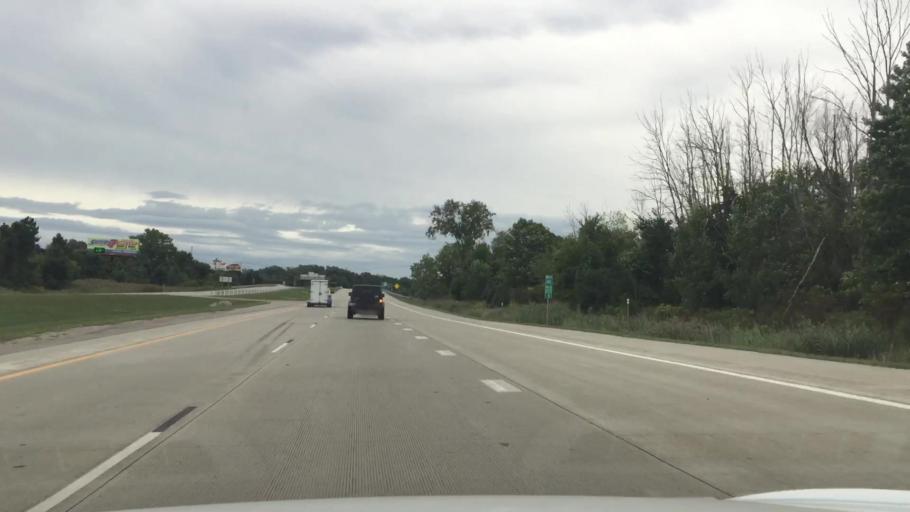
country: US
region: Michigan
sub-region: Saint Clair County
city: Port Huron
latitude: 42.9839
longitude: -82.4752
